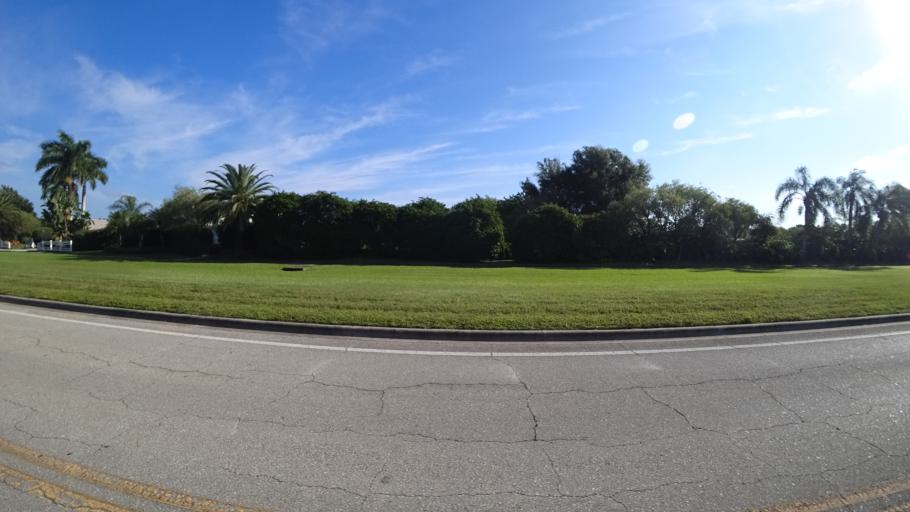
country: US
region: Florida
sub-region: Sarasota County
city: Desoto Lakes
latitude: 27.4203
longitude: -82.4829
